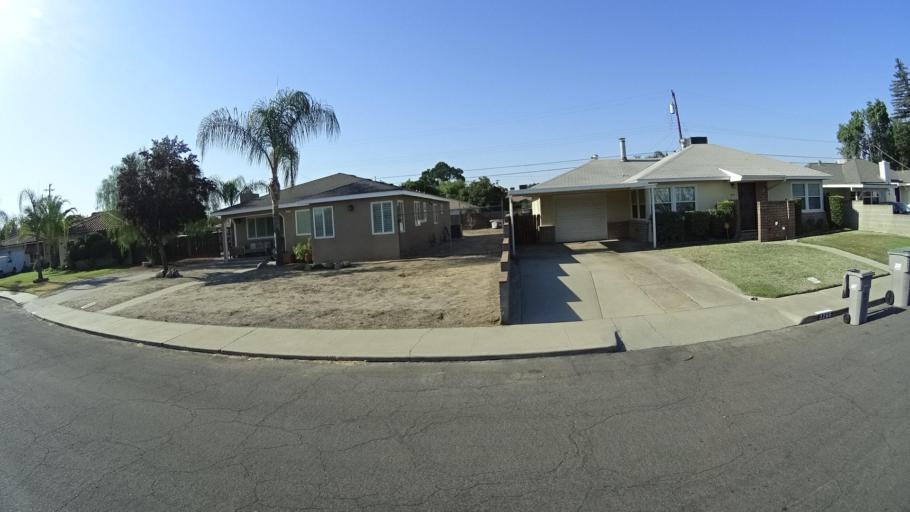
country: US
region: California
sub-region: Fresno County
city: Fresno
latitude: 36.7699
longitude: -119.7686
